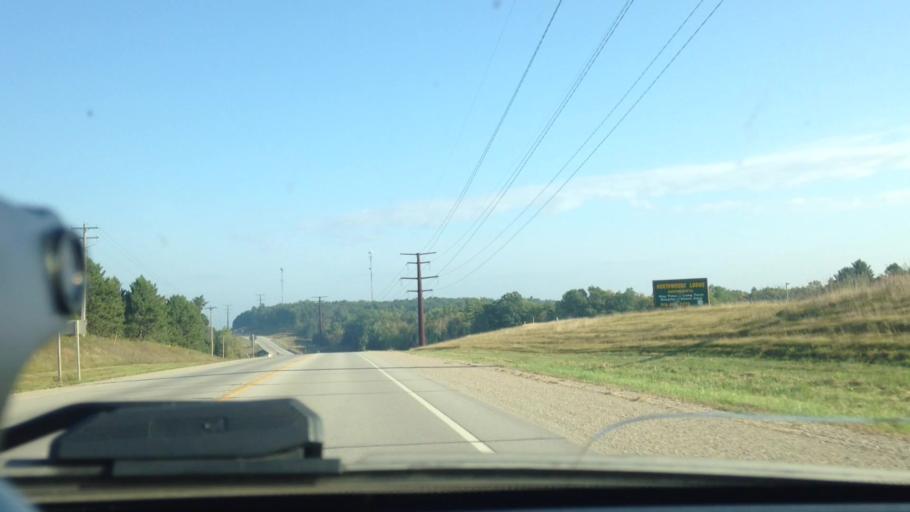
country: US
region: Wisconsin
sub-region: Marinette County
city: Peshtigo
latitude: 45.2040
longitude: -87.9943
